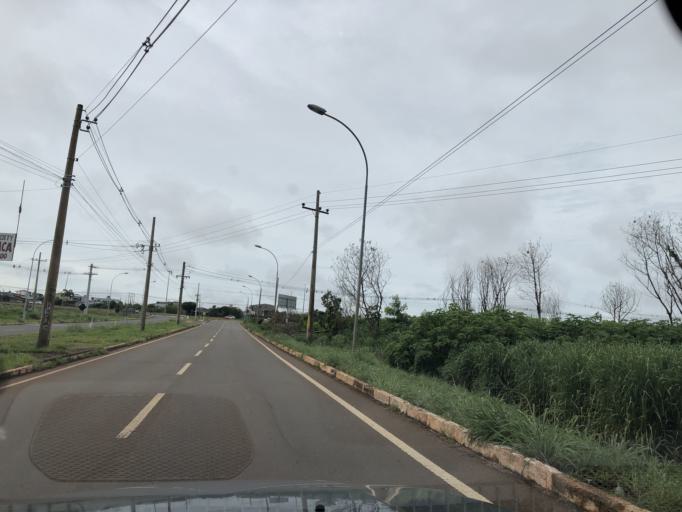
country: BR
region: Federal District
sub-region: Brasilia
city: Brasilia
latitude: -15.7820
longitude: -48.1296
